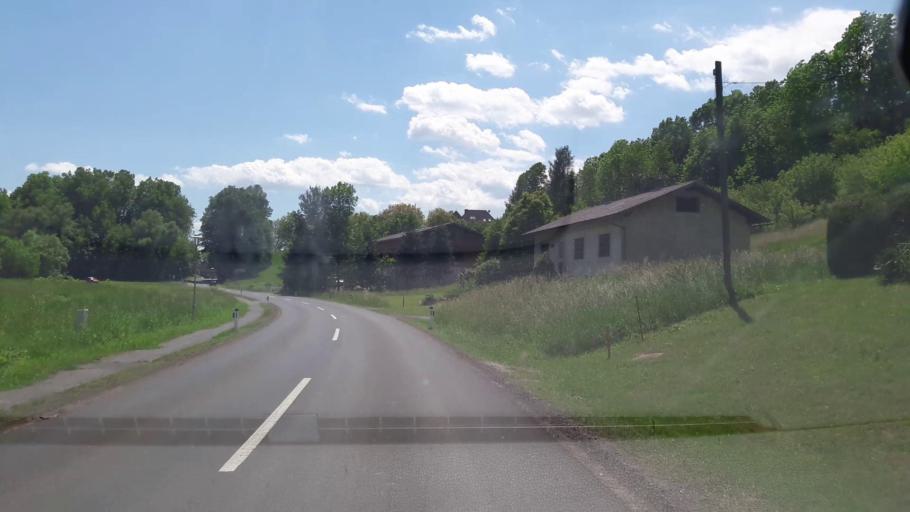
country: AT
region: Burgenland
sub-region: Politischer Bezirk Jennersdorf
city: Jennersdorf
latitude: 46.9403
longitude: 16.1309
